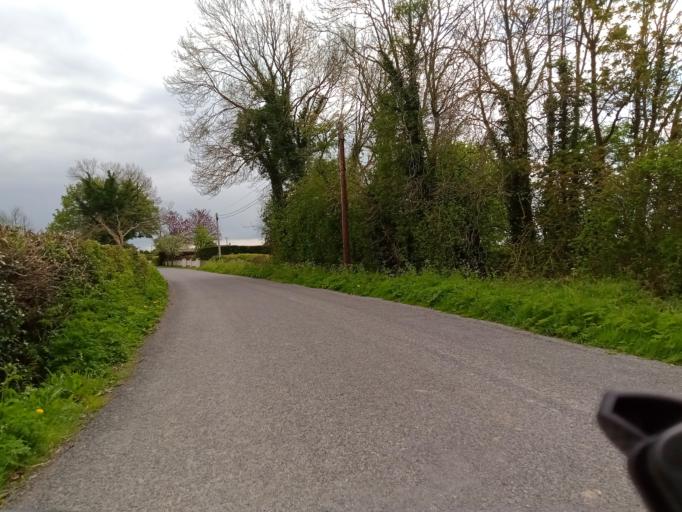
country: IE
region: Leinster
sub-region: Kilkenny
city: Kilkenny
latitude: 52.6136
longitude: -7.2941
